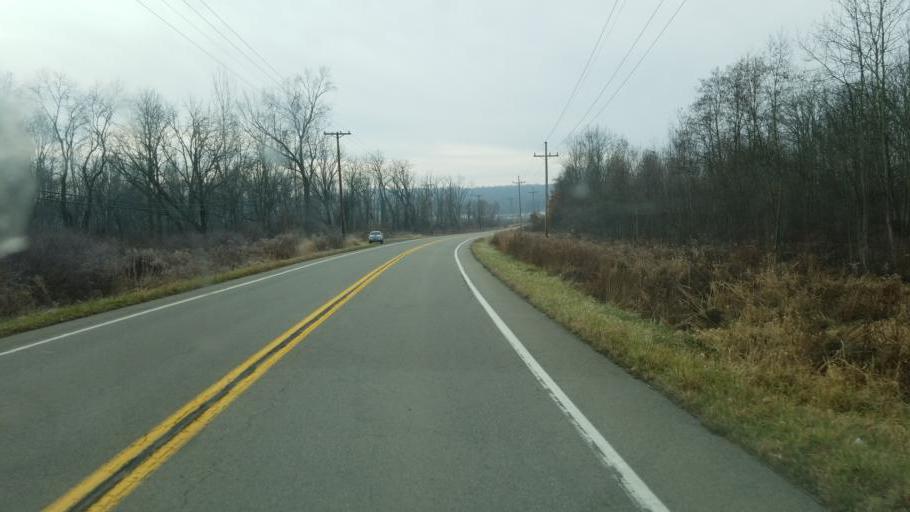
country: US
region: Pennsylvania
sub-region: Crawford County
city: Meadville
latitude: 41.5521
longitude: -80.1843
